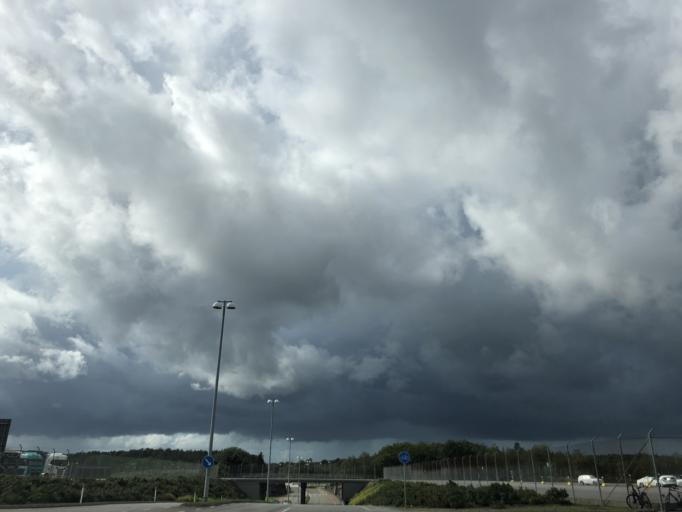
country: SE
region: Vaestra Goetaland
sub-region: Goteborg
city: Torslanda
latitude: 57.7188
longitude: 11.8266
